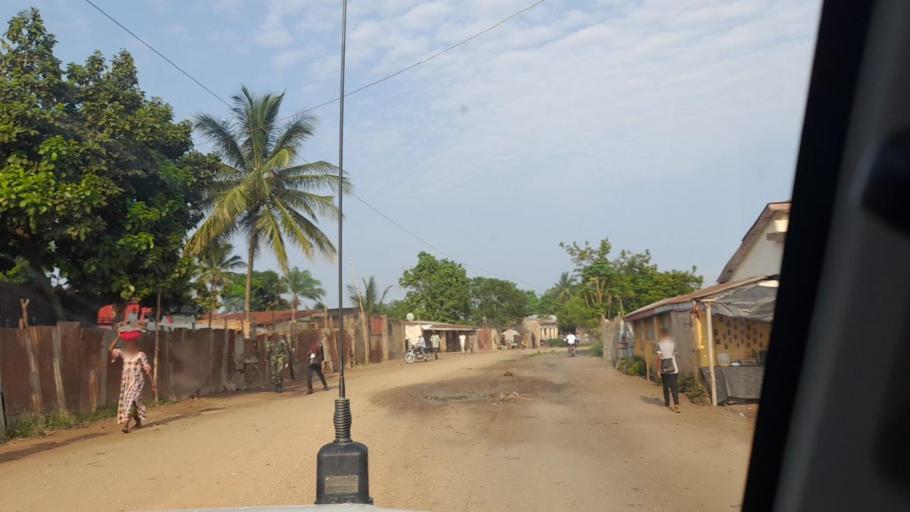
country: CD
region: Kasai-Occidental
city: Kananga
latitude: -5.8950
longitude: 22.3893
